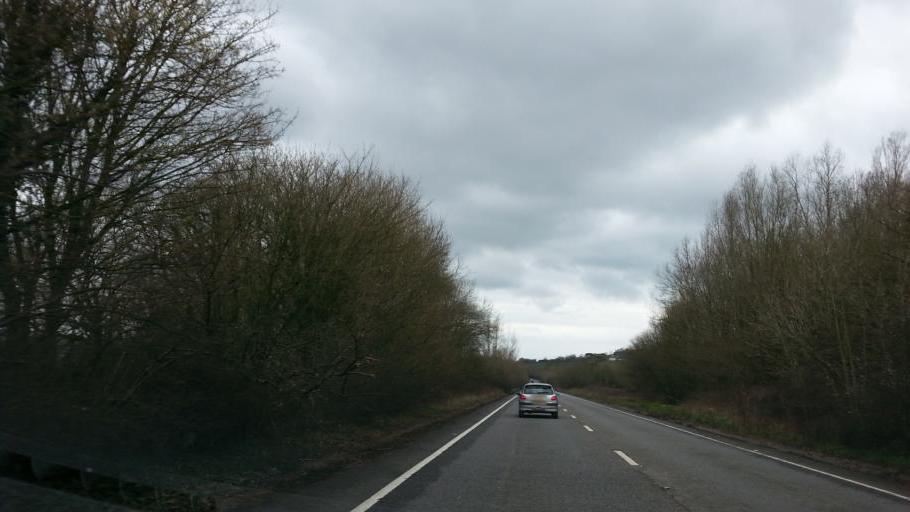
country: GB
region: England
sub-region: Devon
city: Barnstaple
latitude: 51.0630
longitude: -3.9868
